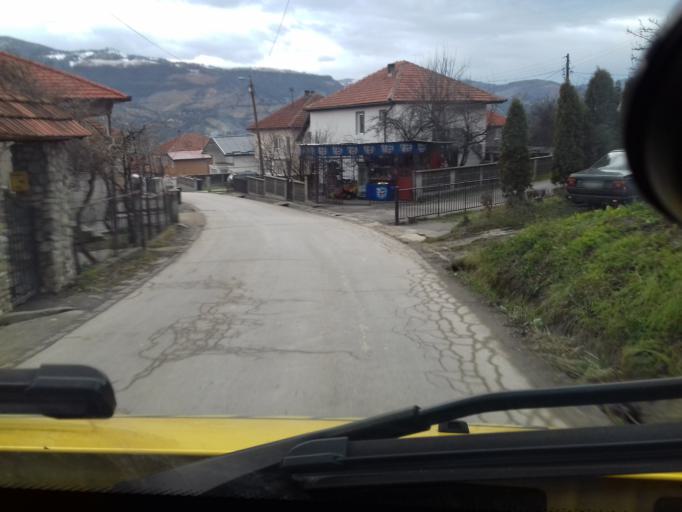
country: BA
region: Federation of Bosnia and Herzegovina
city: Zenica
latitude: 44.1958
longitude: 17.9434
